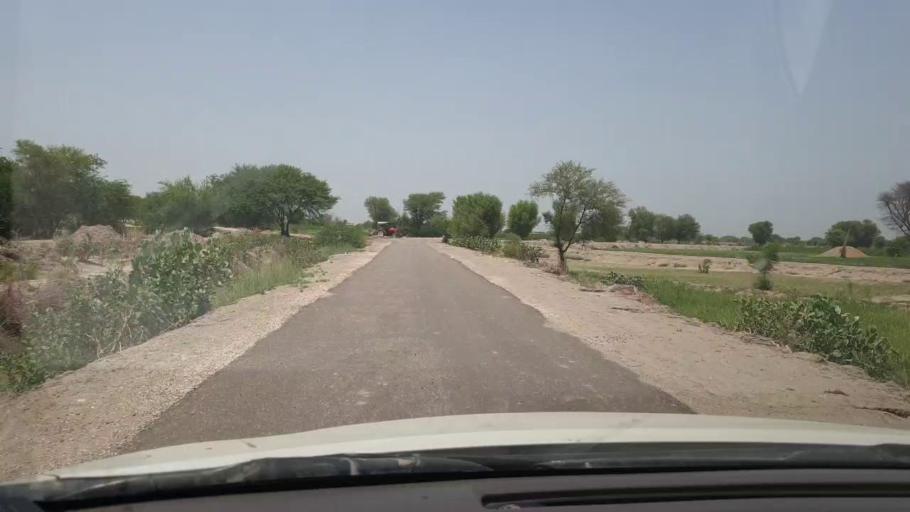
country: PK
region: Sindh
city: Rohri
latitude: 27.5172
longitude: 69.1794
